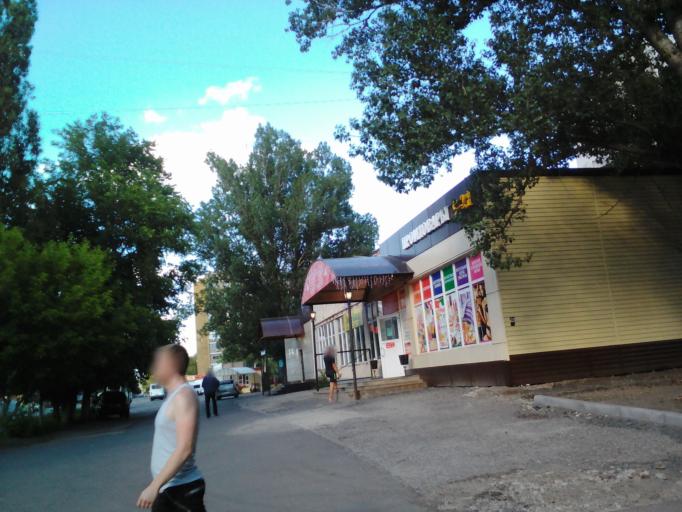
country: RU
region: Kursk
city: Voroshnevo
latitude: 51.6670
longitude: 36.0686
